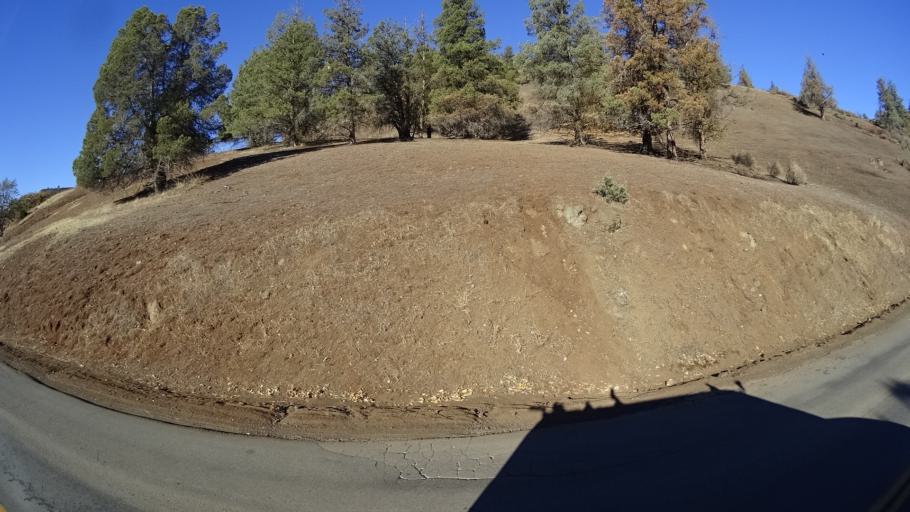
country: US
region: California
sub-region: Siskiyou County
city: Montague
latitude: 41.9290
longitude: -122.4440
